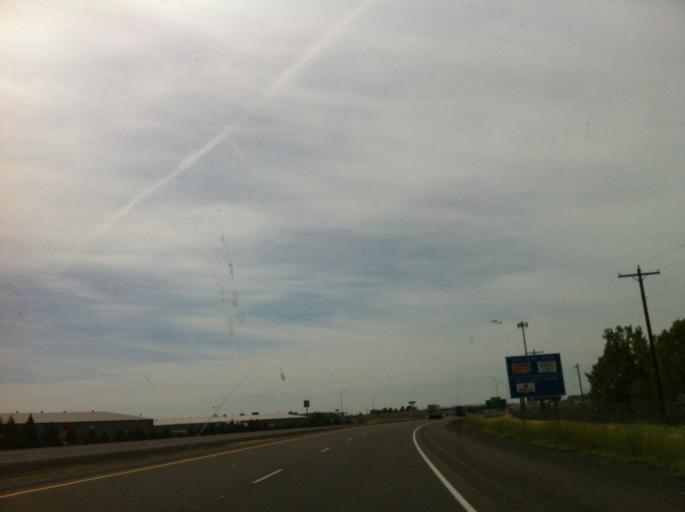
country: US
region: Oregon
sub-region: Malheur County
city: Ontario
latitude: 44.0342
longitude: -116.9554
